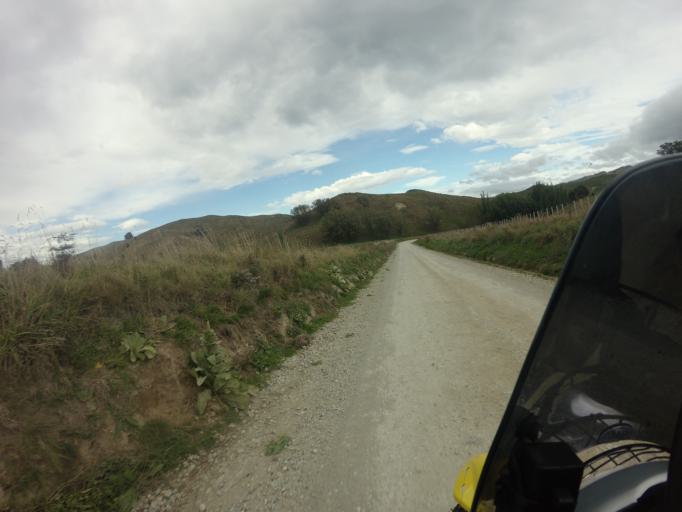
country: NZ
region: Hawke's Bay
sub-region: Wairoa District
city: Wairoa
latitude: -38.6031
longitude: 177.5060
